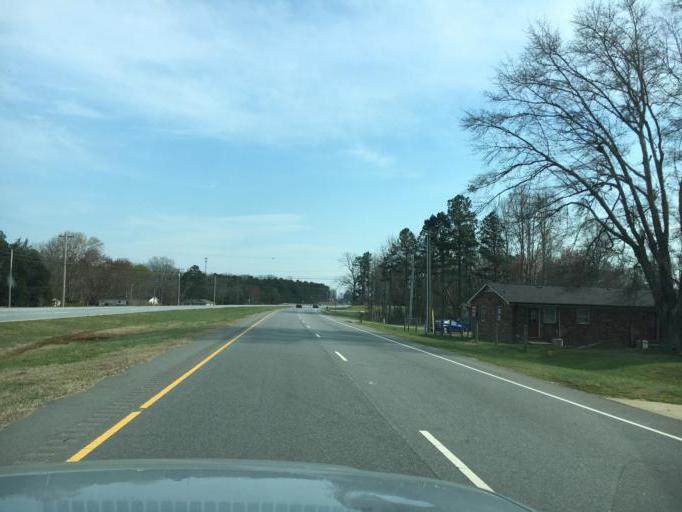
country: US
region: North Carolina
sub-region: Rutherford County
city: Forest City
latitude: 35.2811
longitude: -81.8986
